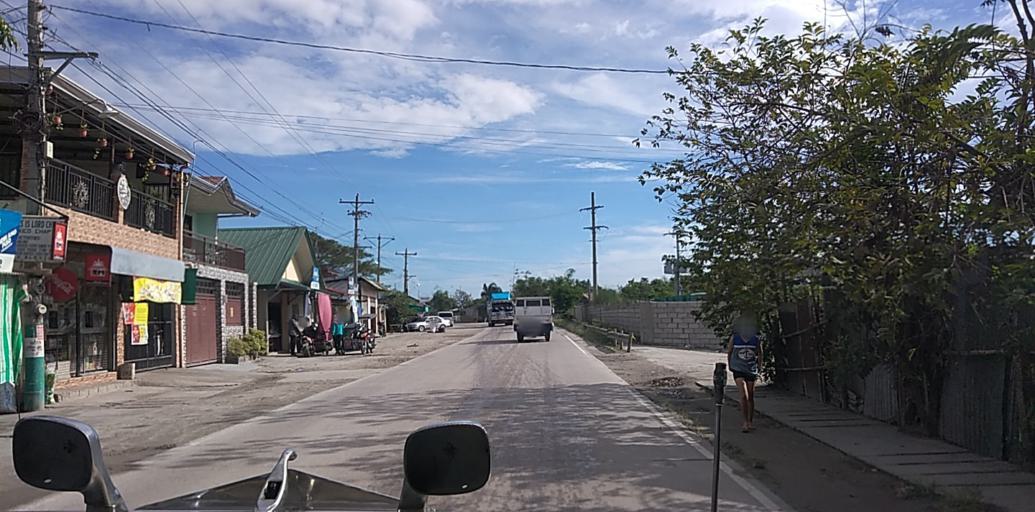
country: PH
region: Central Luzon
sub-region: Province of Pampanga
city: Malino
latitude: 15.1285
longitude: 120.6750
